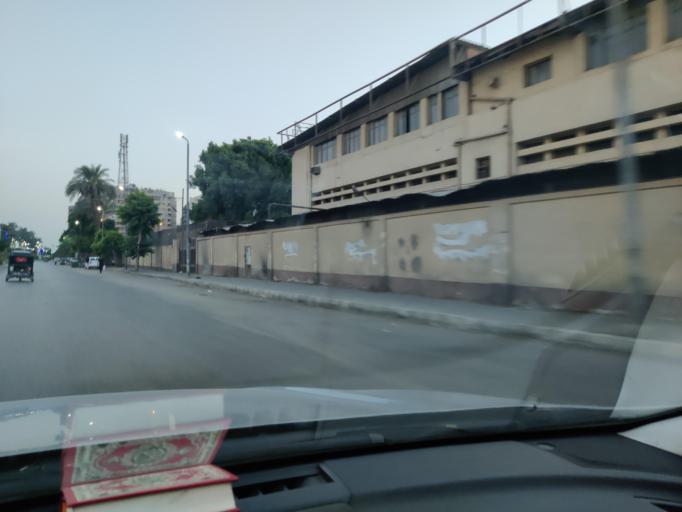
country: EG
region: Muhafazat al Qahirah
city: Cairo
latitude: 30.1052
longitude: 31.3023
